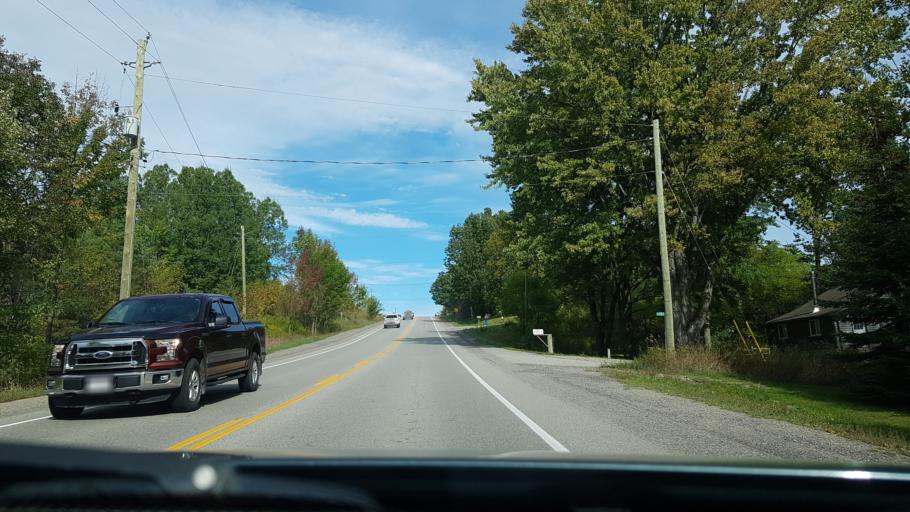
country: CA
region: Ontario
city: Angus
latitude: 44.4823
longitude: -79.8298
